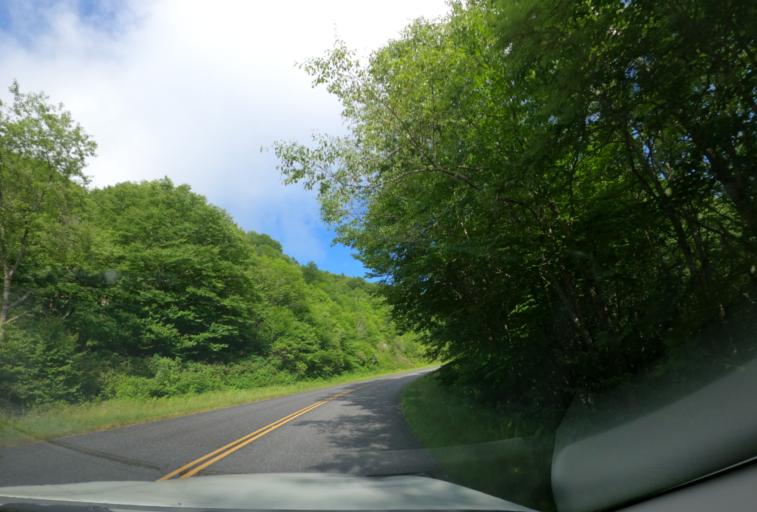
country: US
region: North Carolina
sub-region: Haywood County
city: Hazelwood
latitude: 35.3176
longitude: -82.9614
